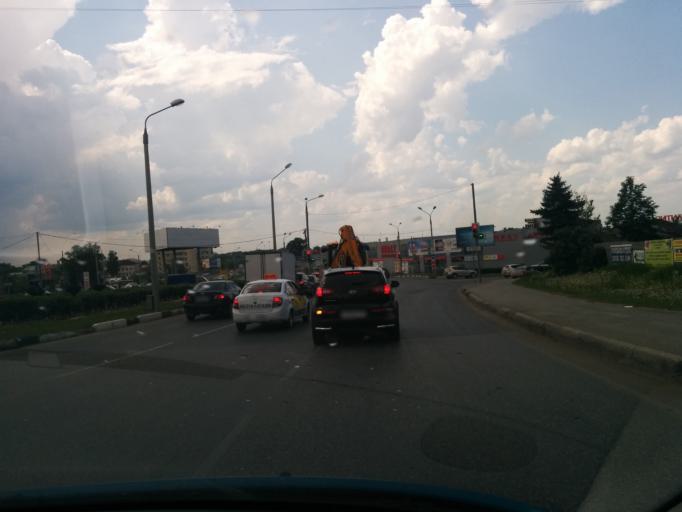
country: RU
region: Perm
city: Kondratovo
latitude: 57.9611
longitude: 56.1355
